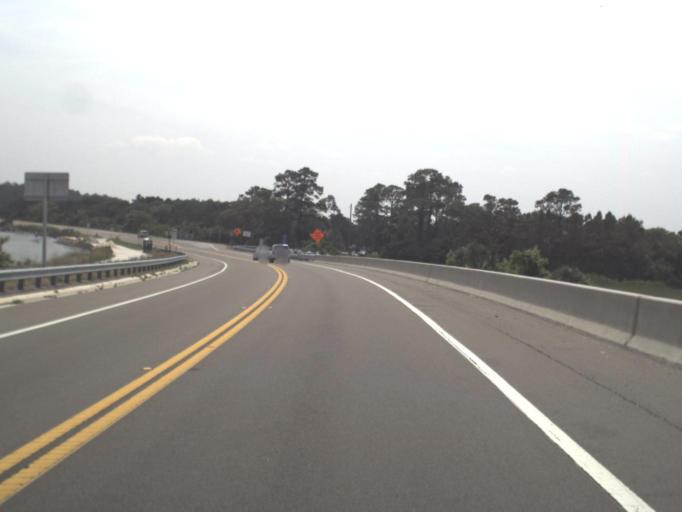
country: US
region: Florida
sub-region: Nassau County
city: Fernandina Beach
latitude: 30.5120
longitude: -81.4575
